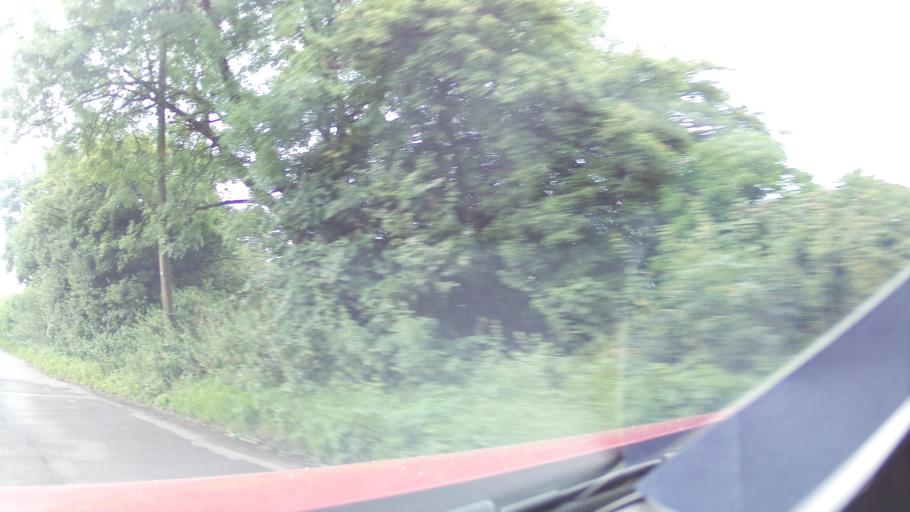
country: GB
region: England
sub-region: Somerset
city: Evercreech
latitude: 51.1764
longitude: -2.5078
